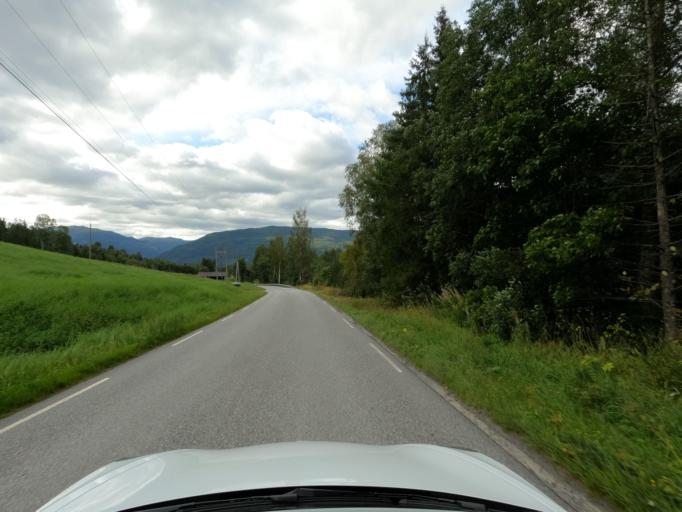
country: NO
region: Telemark
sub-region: Tinn
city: Rjukan
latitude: 60.0039
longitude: 8.8324
